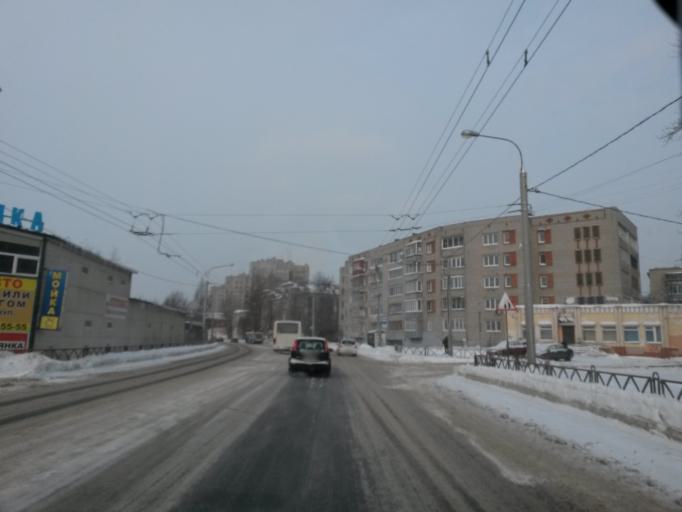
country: RU
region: Jaroslavl
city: Yaroslavl
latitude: 57.6225
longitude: 39.8438
